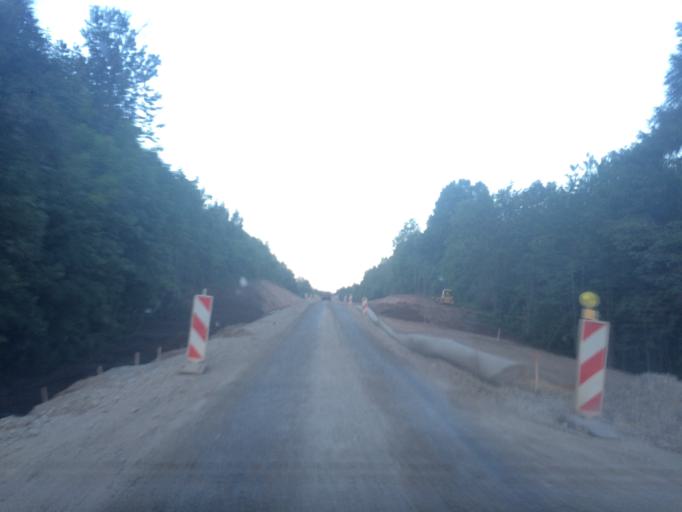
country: LT
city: Zarasai
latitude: 55.7541
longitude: 26.3233
